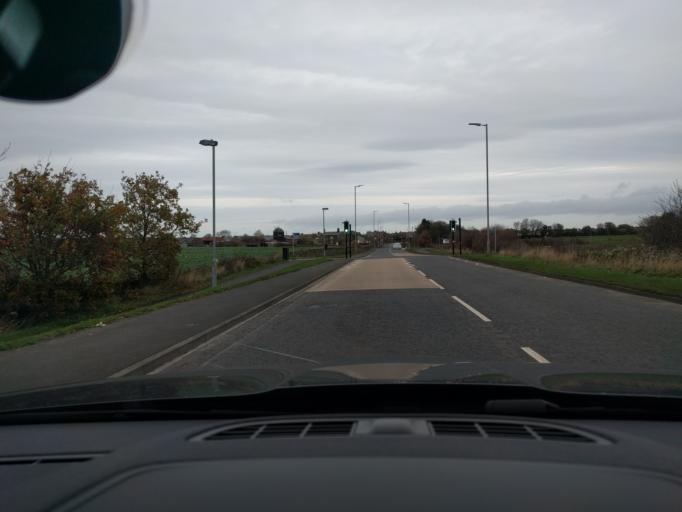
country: GB
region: England
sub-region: Northumberland
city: Newbiggin-by-the-Sea
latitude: 55.1753
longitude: -1.5258
